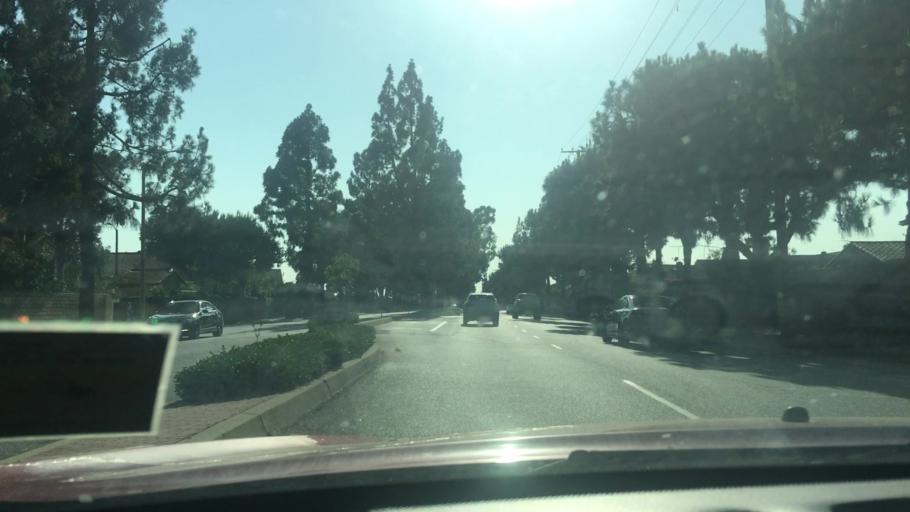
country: US
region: California
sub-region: Los Angeles County
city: Cerritos
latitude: 33.8732
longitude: -118.0663
